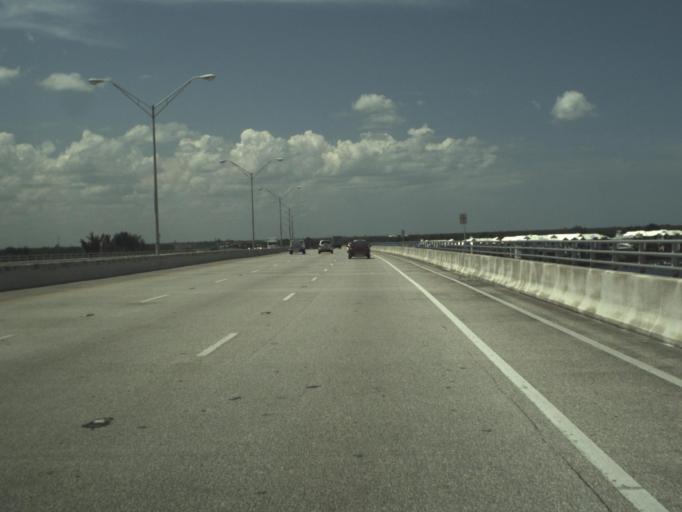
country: US
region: Florida
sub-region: Martin County
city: Stuart
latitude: 27.2081
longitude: -80.2589
